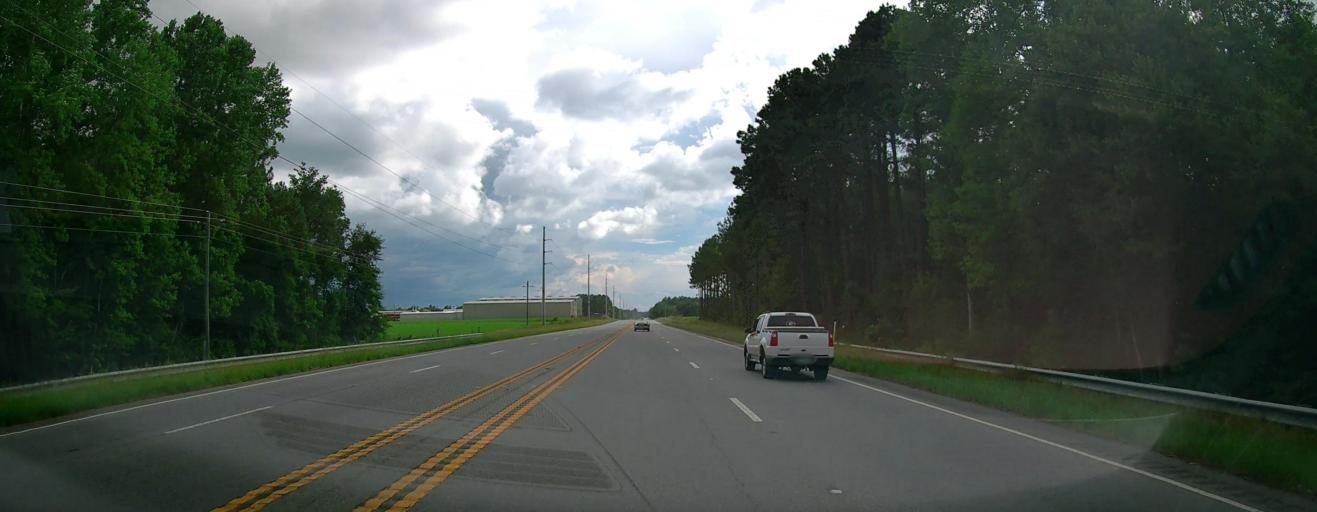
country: US
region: Georgia
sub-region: Pierce County
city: Blackshear
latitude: 31.4035
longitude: -82.1197
